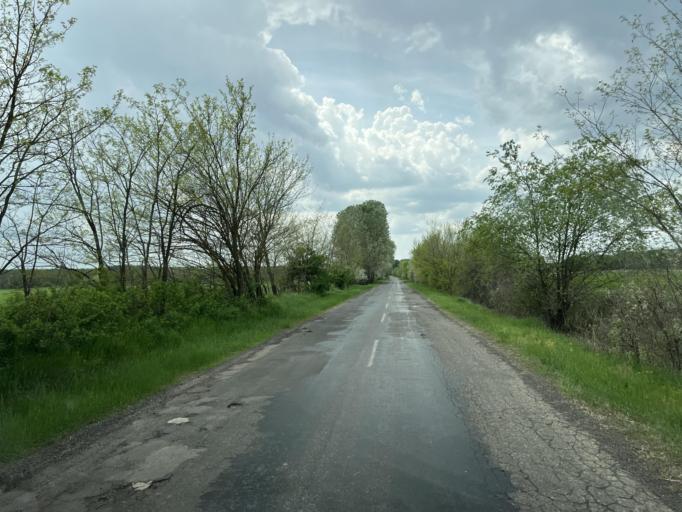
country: HU
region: Pest
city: Csemo
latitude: 47.1185
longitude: 19.7513
